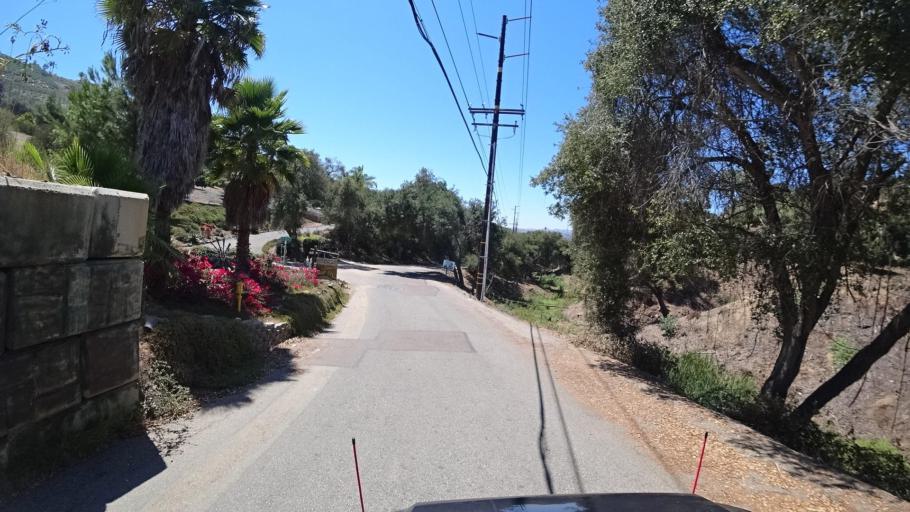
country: US
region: California
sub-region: San Diego County
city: Bonsall
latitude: 33.3386
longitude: -117.1752
